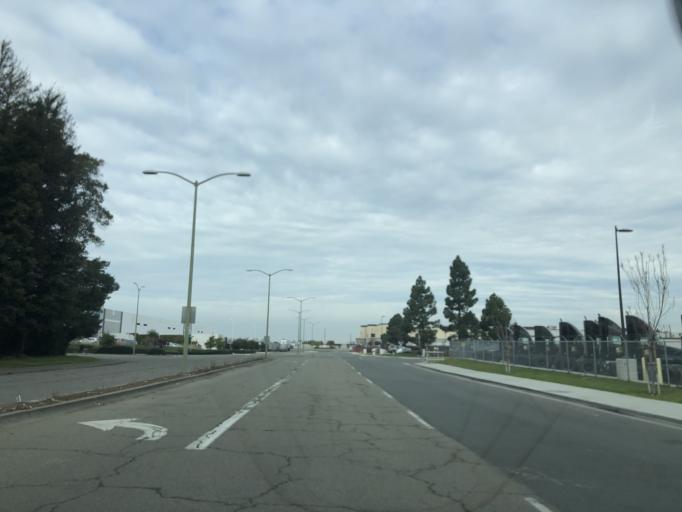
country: US
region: California
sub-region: Alameda County
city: San Leandro
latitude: 37.7322
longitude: -122.2042
